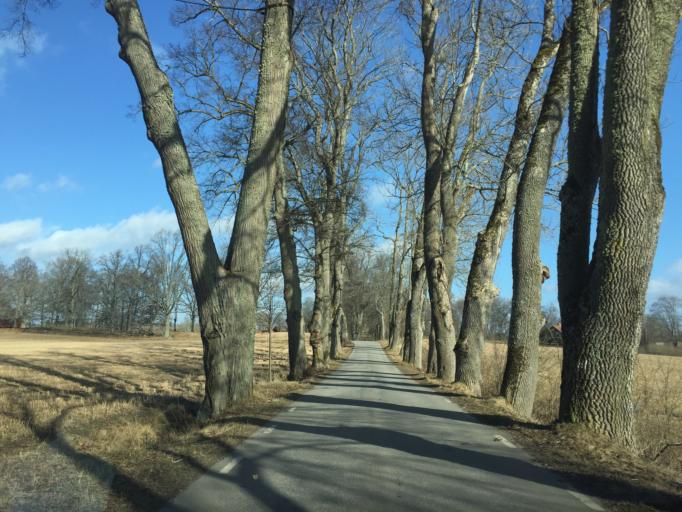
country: SE
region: Soedermanland
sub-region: Vingakers Kommun
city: Vingaker
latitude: 59.0275
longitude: 15.6794
